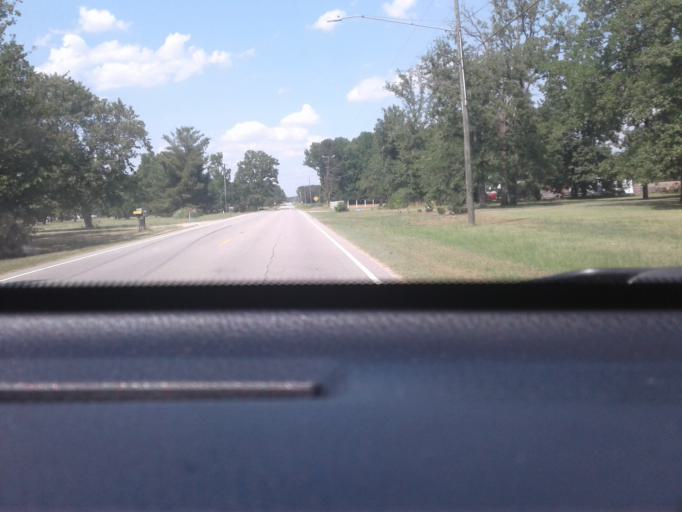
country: US
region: North Carolina
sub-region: Cumberland County
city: Eastover
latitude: 35.1510
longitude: -78.7372
